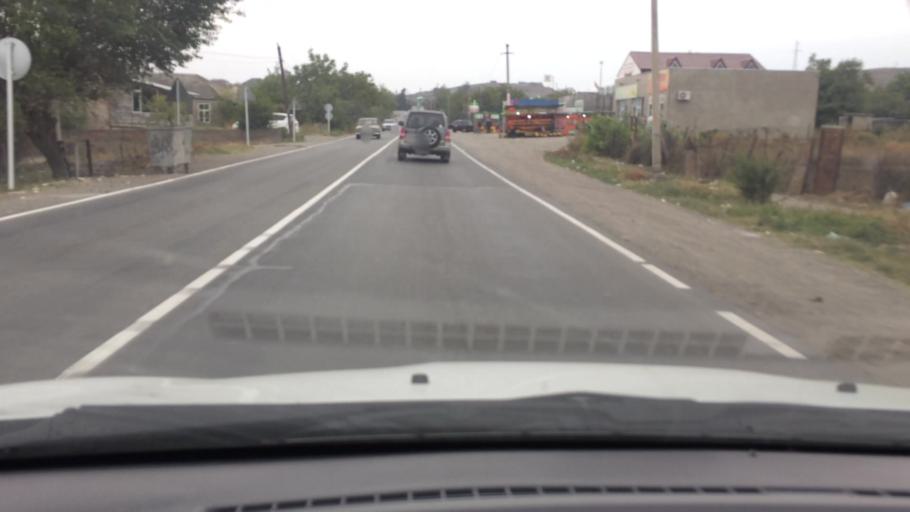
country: GE
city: Naghvarevi
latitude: 41.3758
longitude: 44.8342
